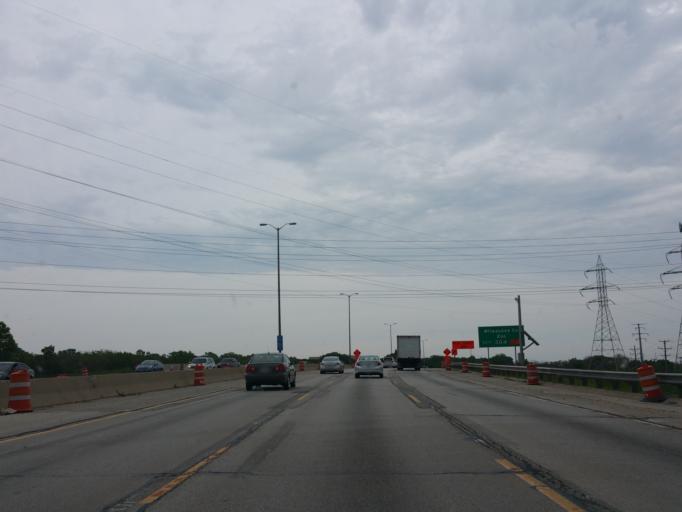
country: US
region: Wisconsin
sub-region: Waukesha County
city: Elm Grove
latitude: 43.0310
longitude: -88.0592
